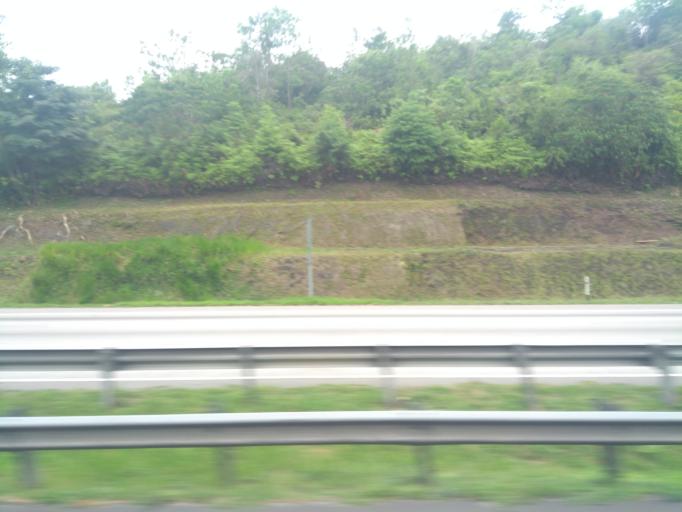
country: MY
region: Negeri Sembilan
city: Tampin
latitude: 2.4666
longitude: 102.1519
